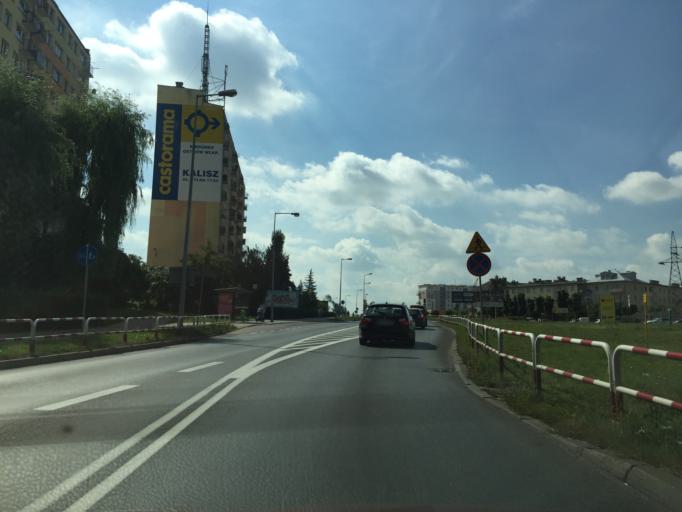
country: PL
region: Greater Poland Voivodeship
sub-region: Kalisz
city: Kalisz
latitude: 51.7527
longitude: 18.0610
